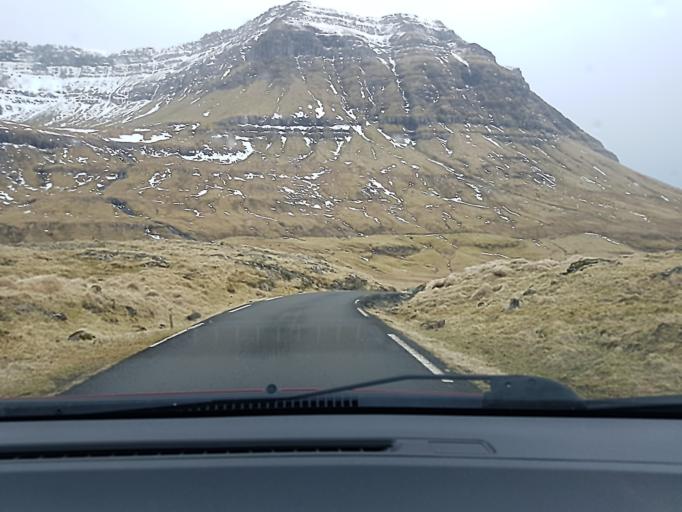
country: FO
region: Streymoy
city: Kollafjordhur
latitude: 62.0431
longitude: -6.9263
